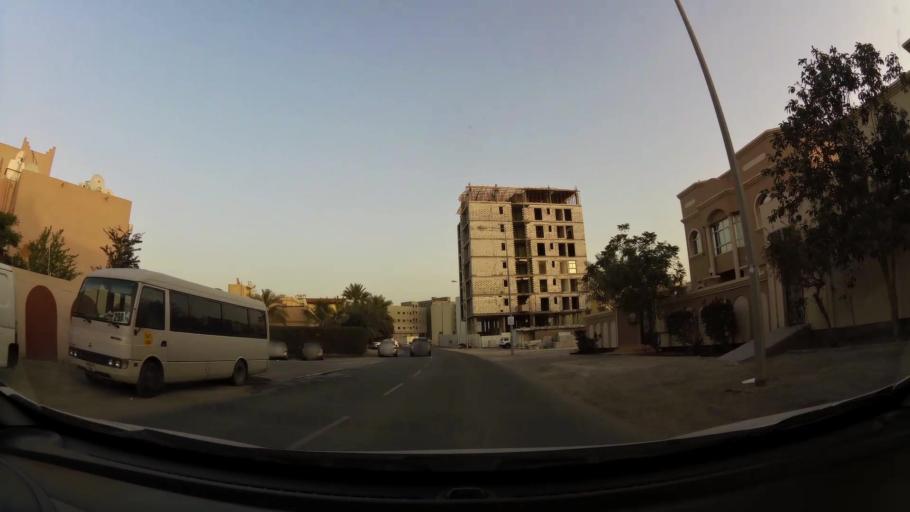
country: BH
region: Northern
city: Madinat `Isa
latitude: 26.1919
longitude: 50.4816
